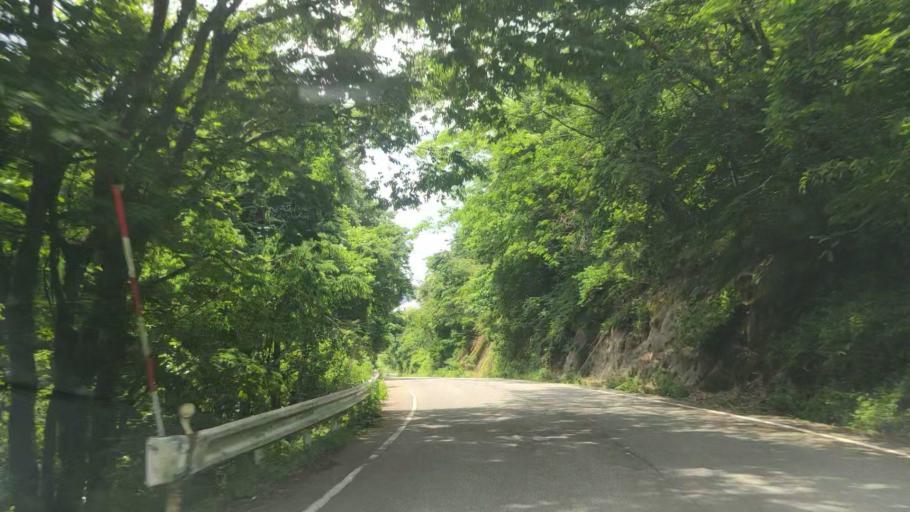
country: JP
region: Hyogo
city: Toyooka
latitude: 35.5088
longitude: 134.6852
